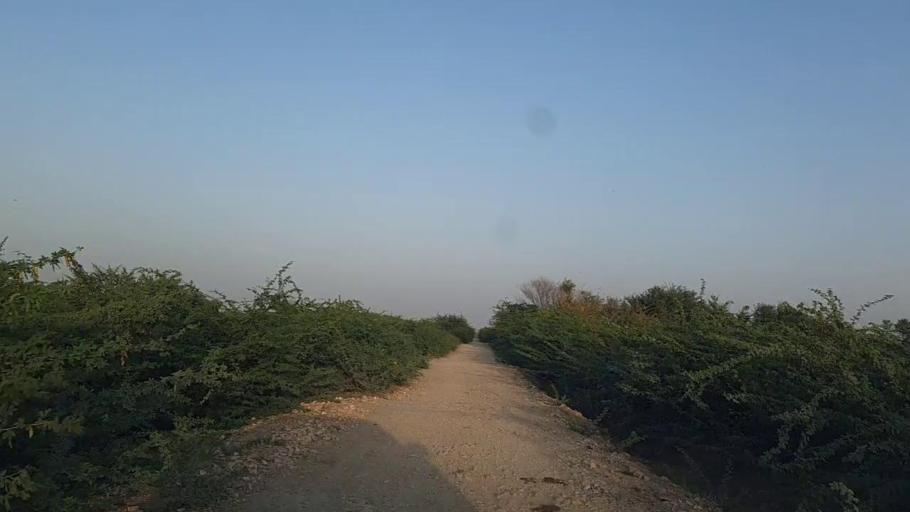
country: PK
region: Sindh
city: Naukot
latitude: 24.6970
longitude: 69.2462
